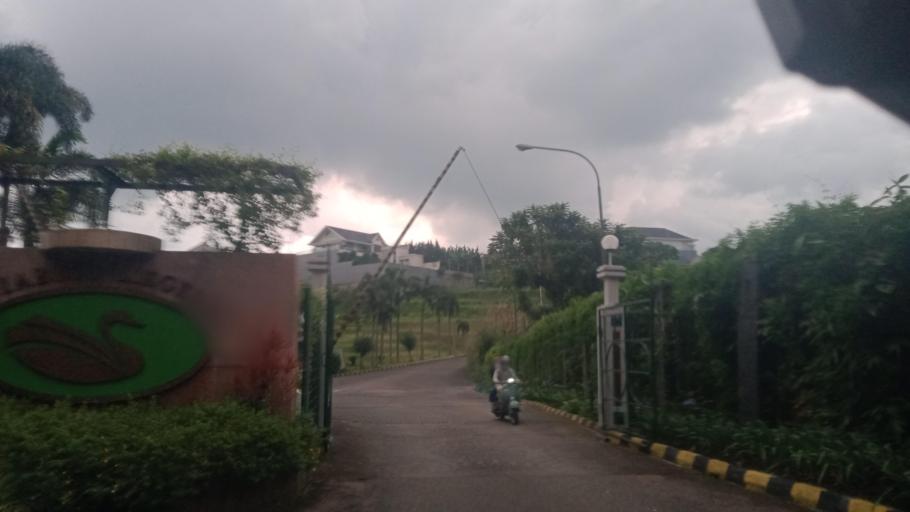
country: ID
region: West Java
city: Lembang
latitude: -6.8488
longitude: 107.5907
